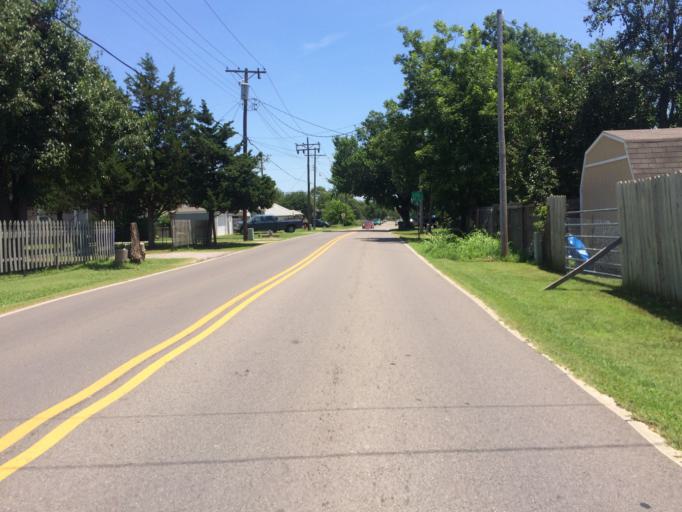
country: US
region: Oklahoma
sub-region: Cleveland County
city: Norman
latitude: 35.2256
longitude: -97.4511
